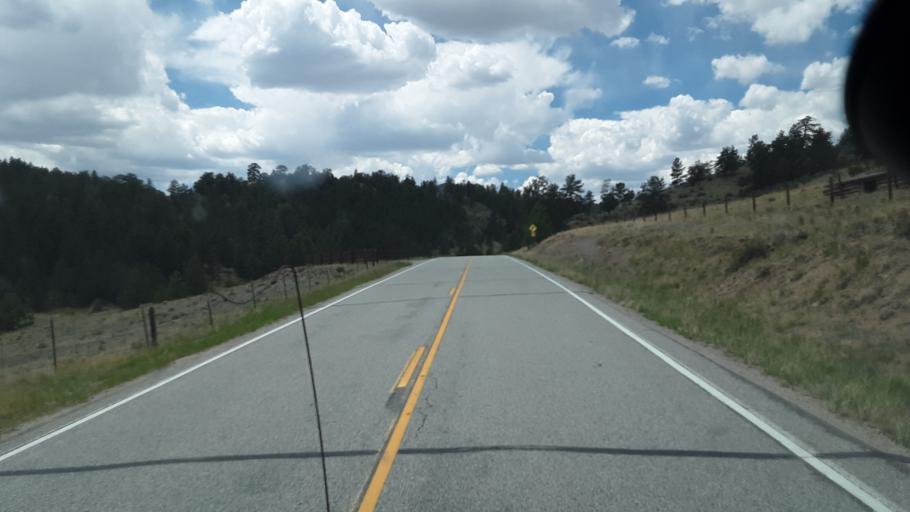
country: US
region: Colorado
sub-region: Teller County
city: Cripple Creek
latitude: 38.7843
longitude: -105.5790
